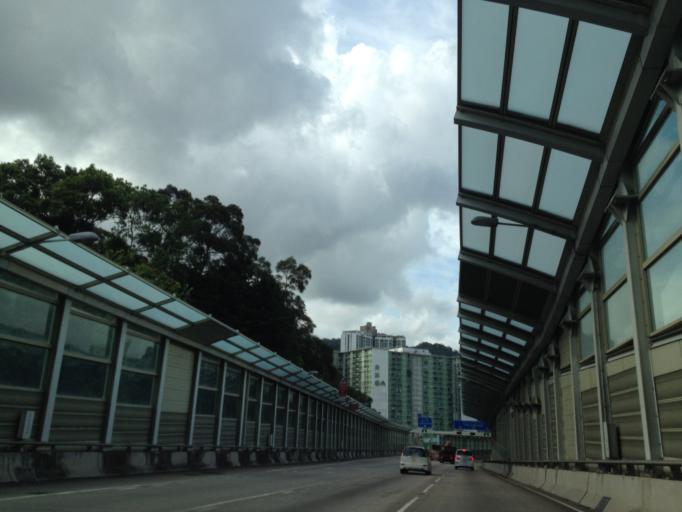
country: HK
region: Sha Tin
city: Sha Tin
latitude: 22.3741
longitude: 114.1754
